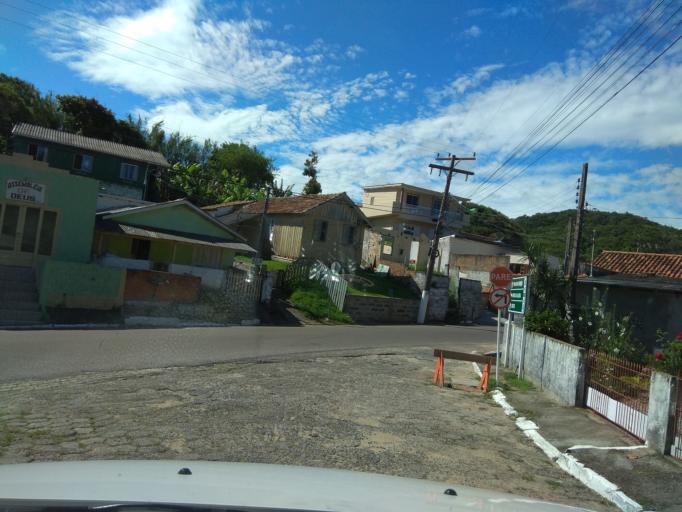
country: BR
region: Santa Catarina
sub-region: Laguna
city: Laguna
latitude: -28.4825
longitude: -48.7756
